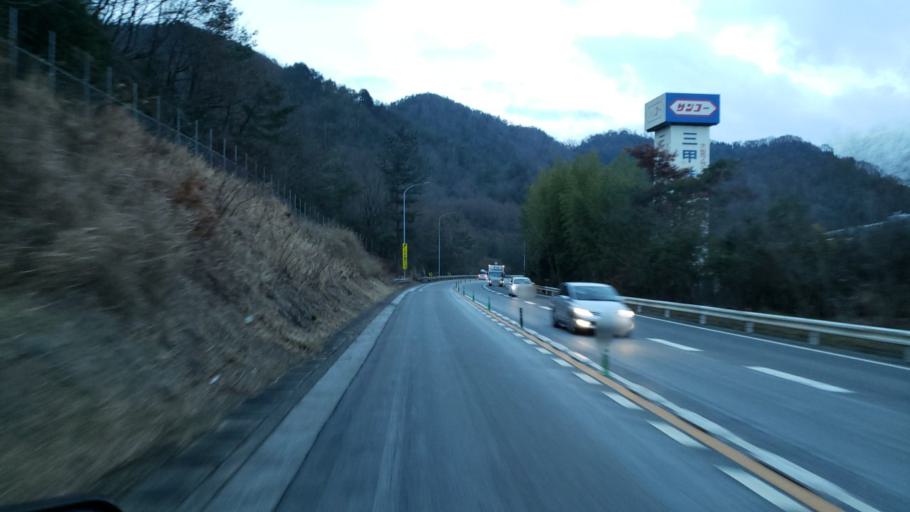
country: JP
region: Hyogo
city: Nishiwaki
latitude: 35.0195
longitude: 134.7662
